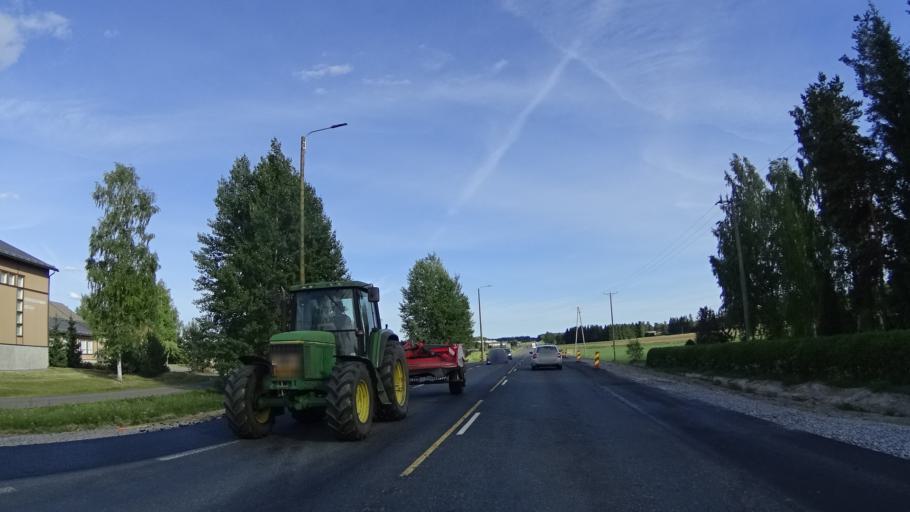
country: FI
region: Haeme
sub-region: Forssa
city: Forssa
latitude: 60.7675
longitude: 23.6841
